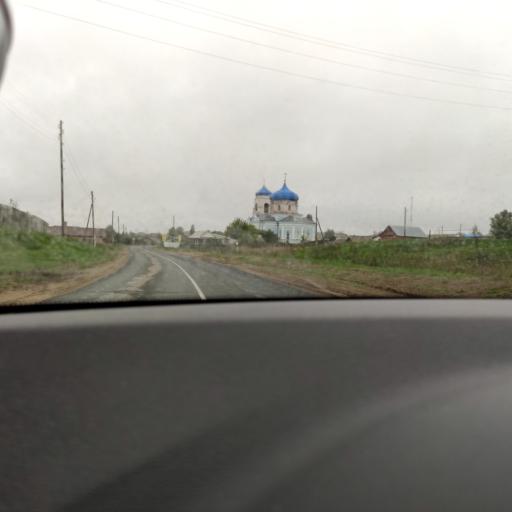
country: RU
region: Samara
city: Yelkhovka
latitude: 53.7433
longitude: 50.2649
